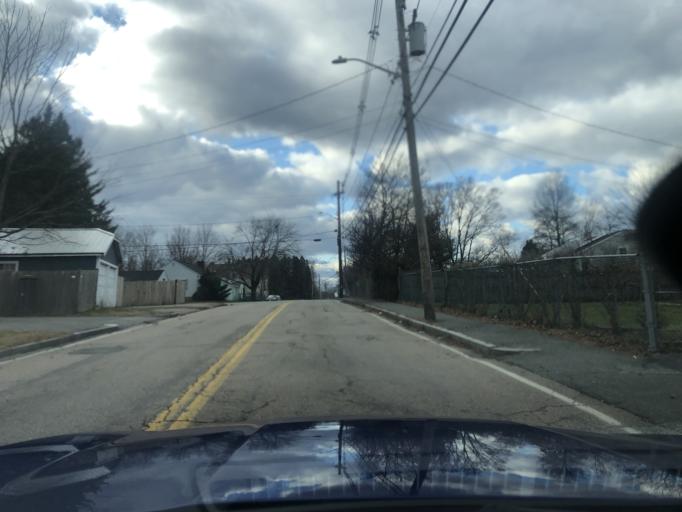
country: US
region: Massachusetts
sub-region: Plymouth County
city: Brockton
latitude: 42.0979
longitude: -71.0273
